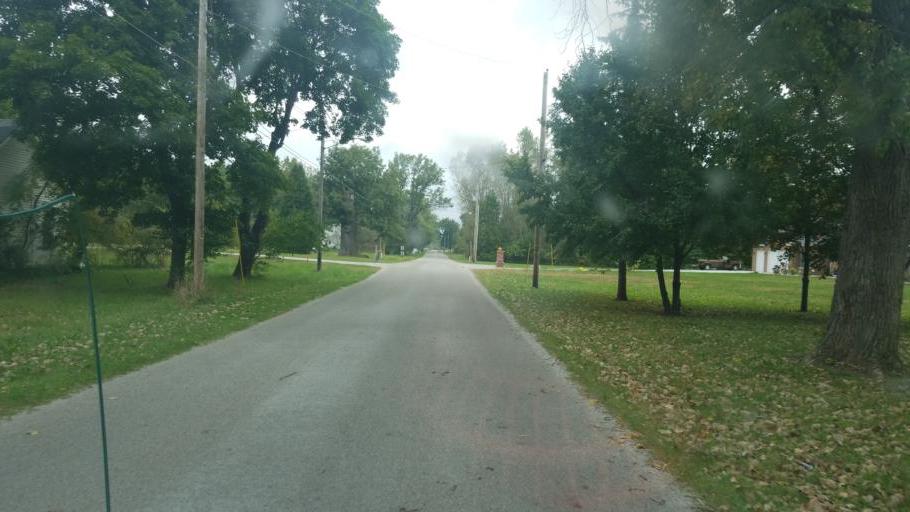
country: US
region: Ohio
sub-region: Wood County
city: Bowling Green
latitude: 41.3002
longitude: -83.6696
